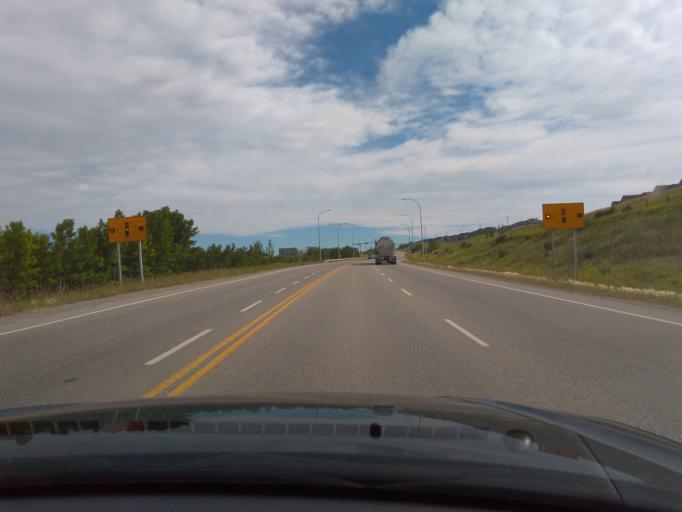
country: CA
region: Alberta
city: Cochrane
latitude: 51.2126
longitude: -114.4743
